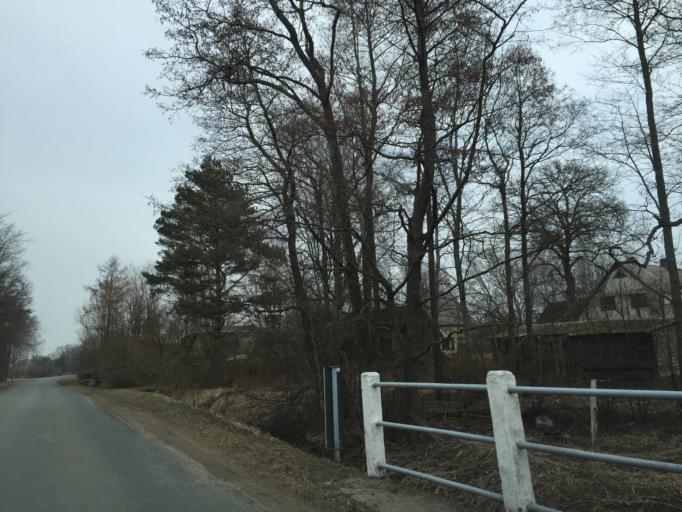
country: LV
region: Salacgrivas
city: Ainazi
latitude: 57.9991
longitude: 24.4340
